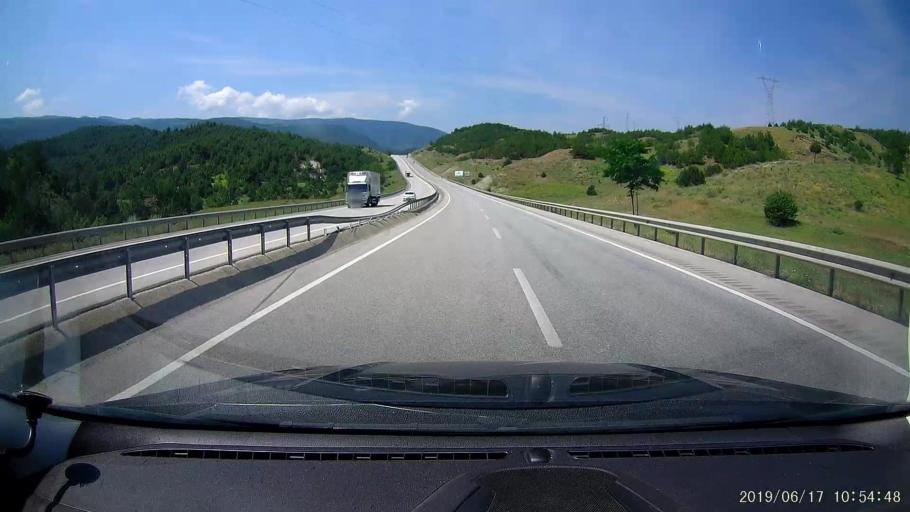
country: TR
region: Corum
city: Hacihamza
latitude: 41.0666
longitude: 34.2928
